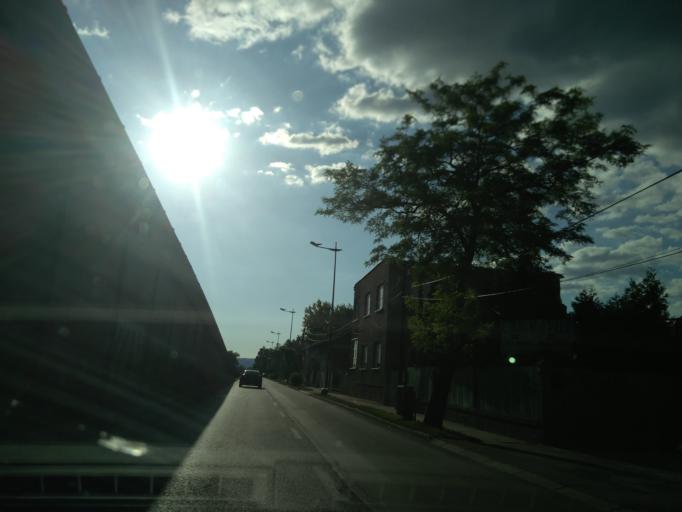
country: HU
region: Budapest
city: Budapest X. keruelet
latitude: 47.4637
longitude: 19.1620
